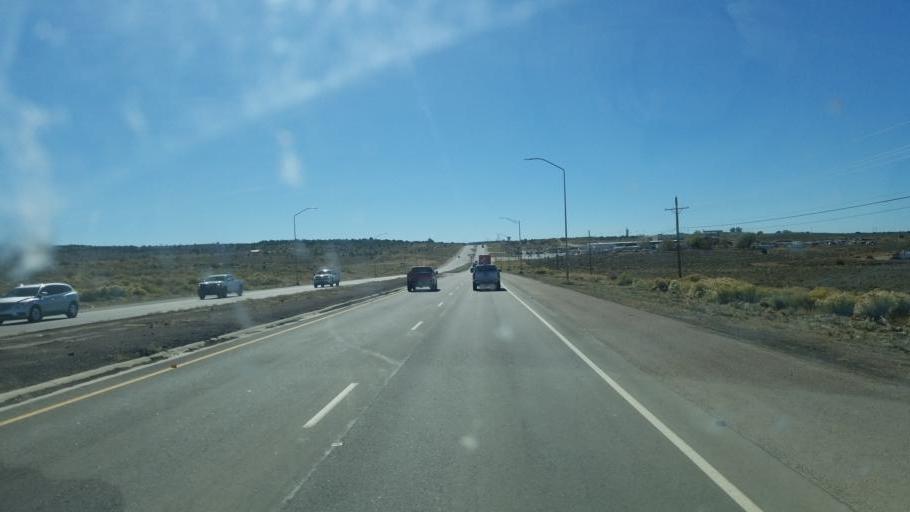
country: US
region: New Mexico
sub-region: McKinley County
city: Gallup
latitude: 35.6132
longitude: -108.7782
